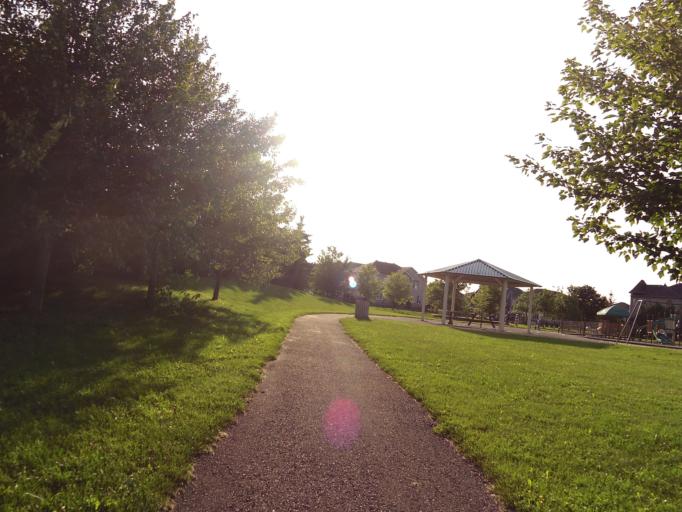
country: CA
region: Ontario
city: Ottawa
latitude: 45.3606
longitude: -75.6943
